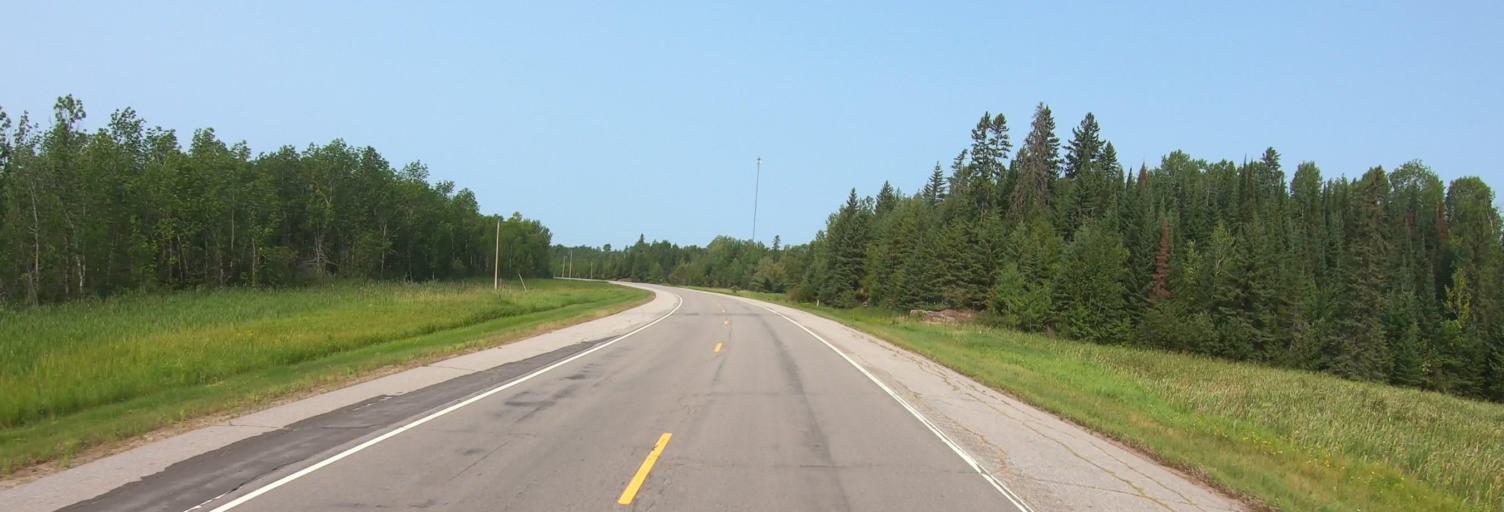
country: US
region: Minnesota
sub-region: Saint Louis County
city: Mountain Iron
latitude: 48.0910
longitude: -92.8266
